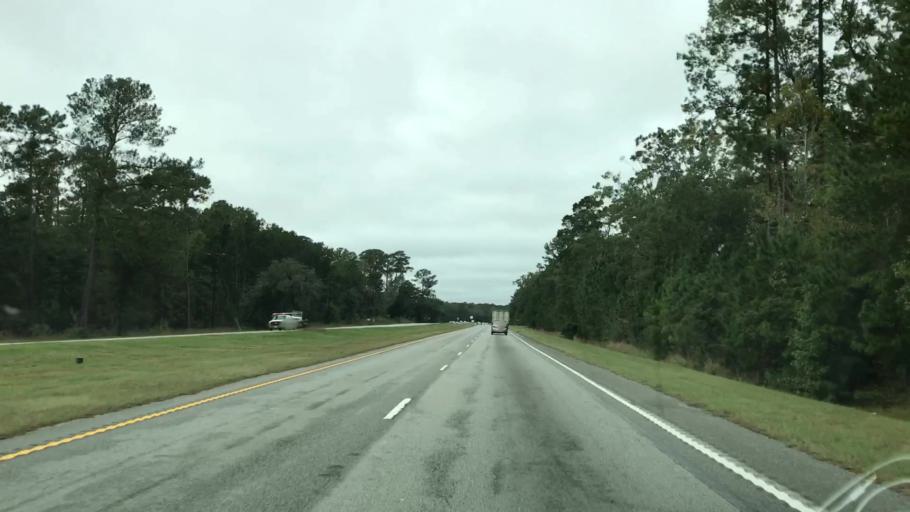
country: US
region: South Carolina
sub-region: Beaufort County
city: Laurel Bay
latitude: 32.3715
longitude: -80.8534
